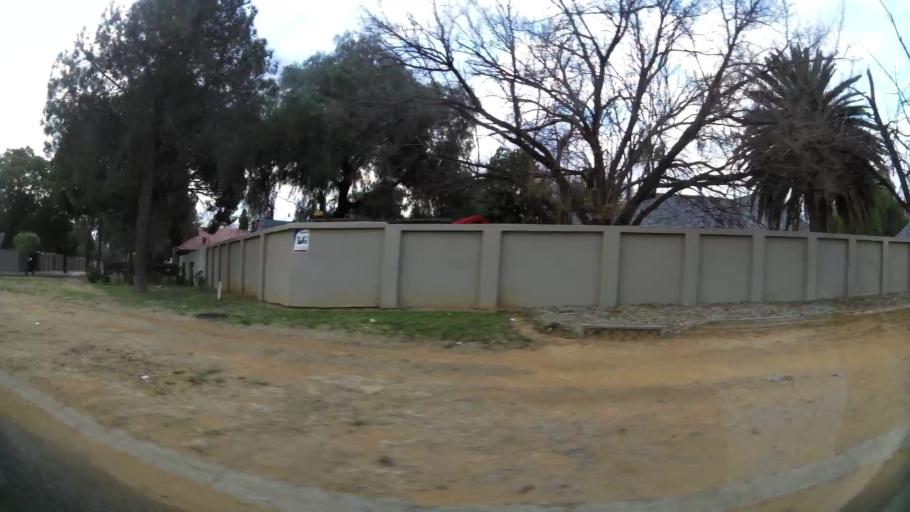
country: ZA
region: Orange Free State
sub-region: Lejweleputswa District Municipality
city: Welkom
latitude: -27.9887
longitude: 26.7272
